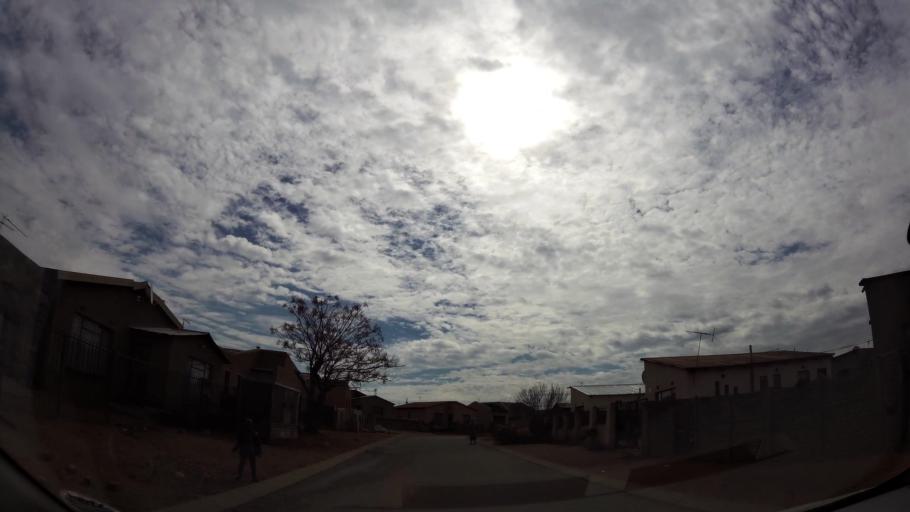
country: ZA
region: Gauteng
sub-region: Ekurhuleni Metropolitan Municipality
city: Germiston
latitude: -26.3800
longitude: 28.1658
